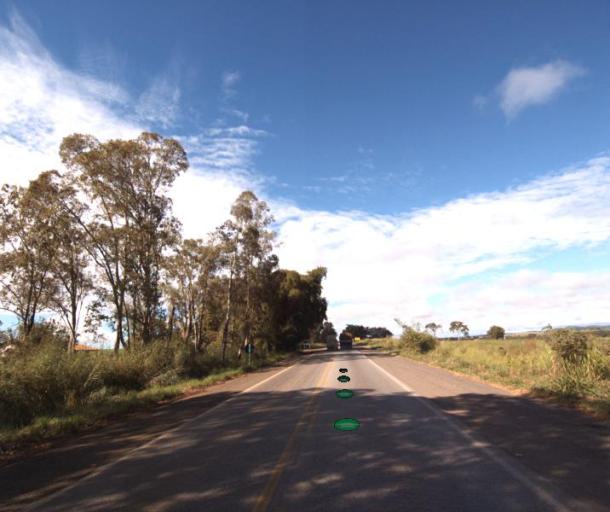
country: BR
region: Goias
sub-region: Uruacu
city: Uruacu
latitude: -14.6268
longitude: -49.1731
